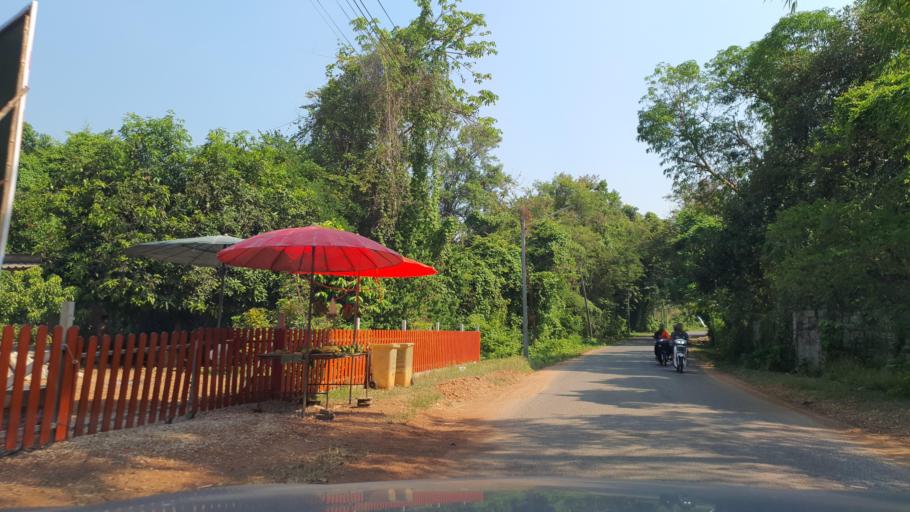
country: TH
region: Kanchanaburi
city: Kanchanaburi
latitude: 14.0704
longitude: 99.4846
